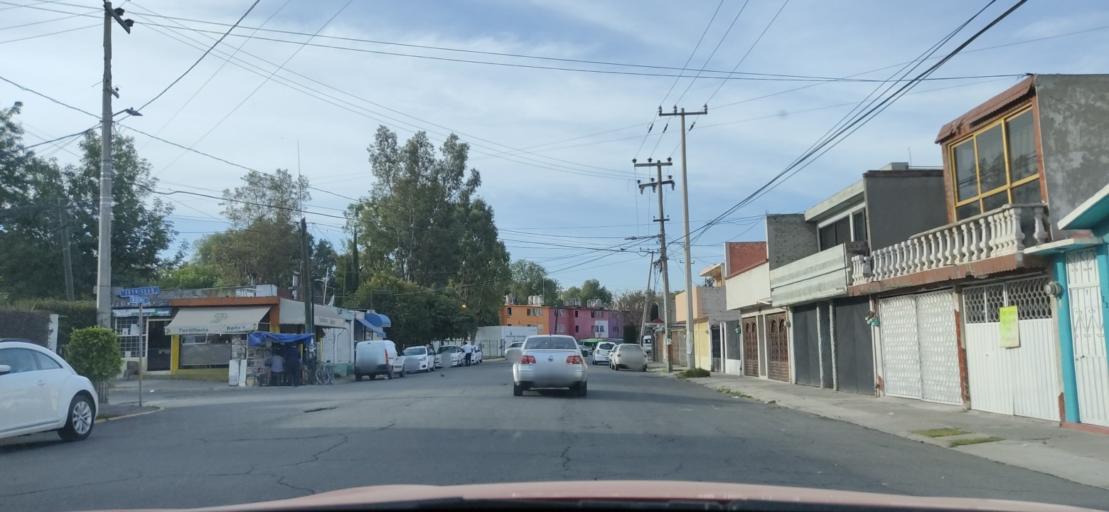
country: MX
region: Mexico
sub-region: Cuautitlan
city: San Jose del Puente
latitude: 19.6906
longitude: -99.2068
